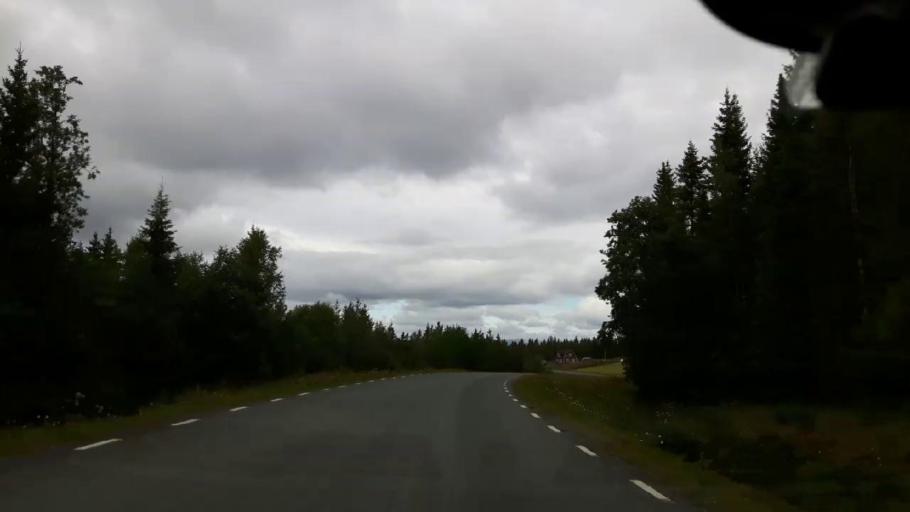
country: SE
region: Jaemtland
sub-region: Krokoms Kommun
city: Valla
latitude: 63.5405
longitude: 13.8567
